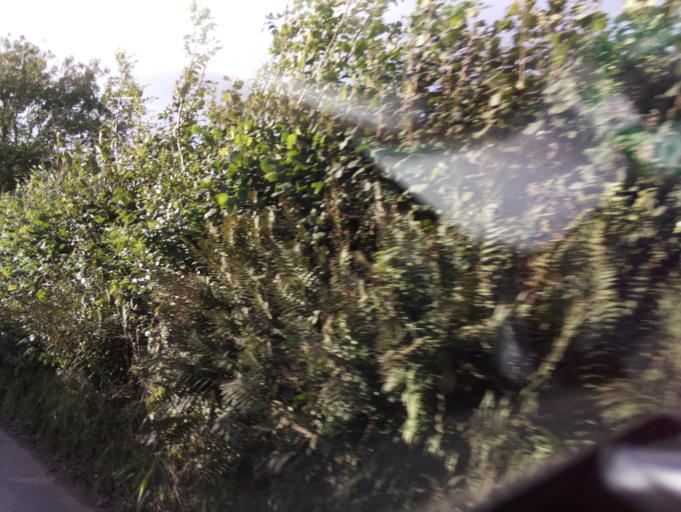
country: GB
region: England
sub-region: Devon
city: Totnes
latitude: 50.3630
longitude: -3.7368
